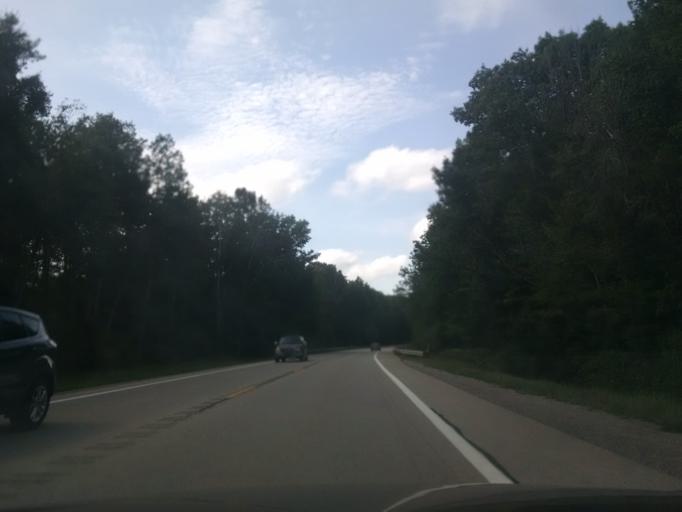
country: US
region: Michigan
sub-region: Clare County
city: Clare
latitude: 43.8715
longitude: -84.9379
